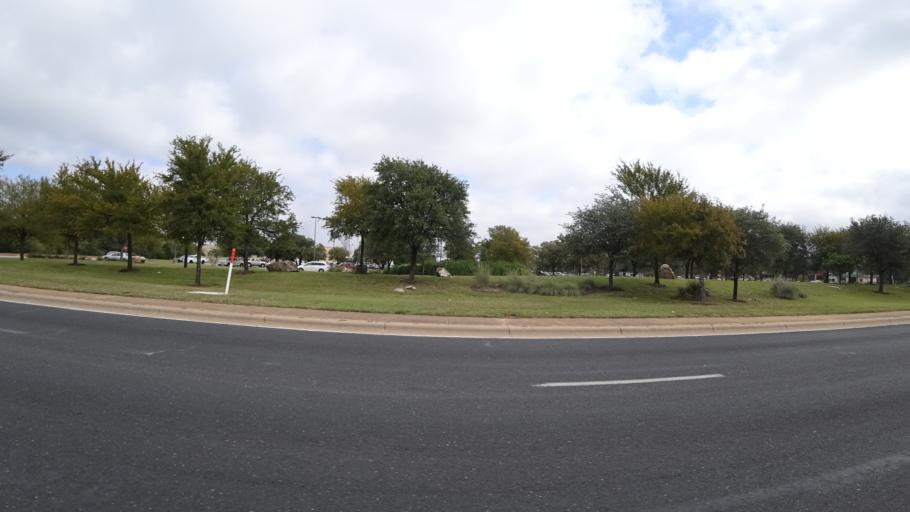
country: US
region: Texas
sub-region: Travis County
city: Shady Hollow
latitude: 30.2144
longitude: -97.8314
